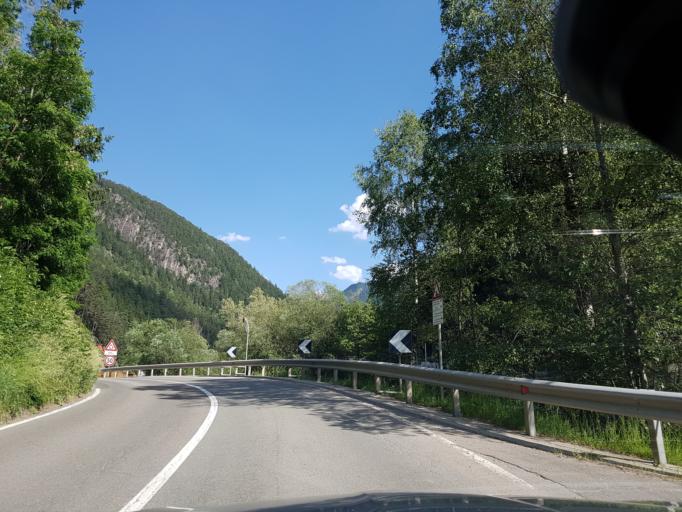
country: IT
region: Trentino-Alto Adige
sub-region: Bolzano
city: Ortisei
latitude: 46.5857
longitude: 11.6314
